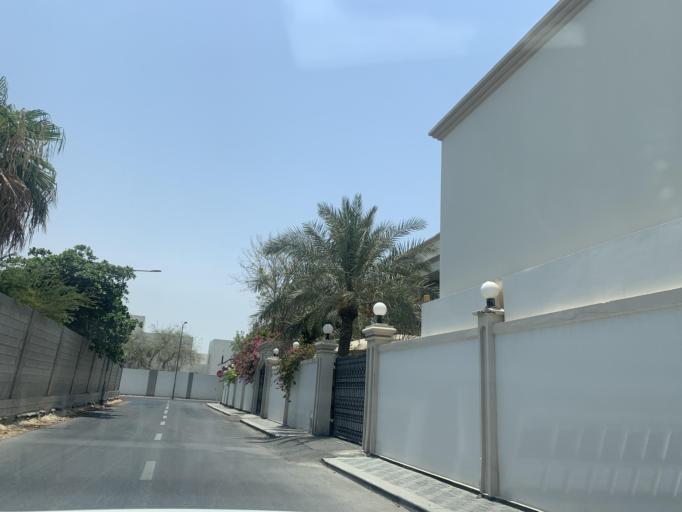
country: BH
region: Manama
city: Jidd Hafs
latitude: 26.2081
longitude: 50.4777
